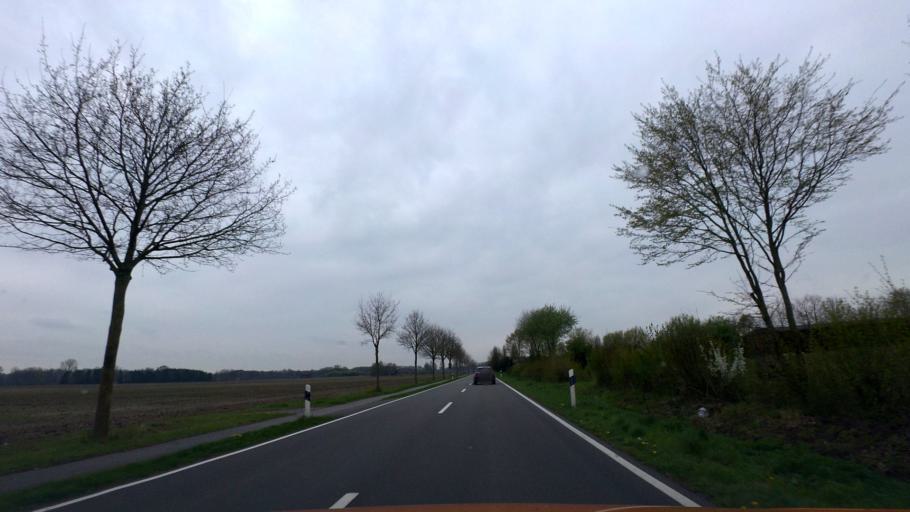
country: DE
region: Lower Saxony
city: Bakum
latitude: 52.7094
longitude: 8.2020
